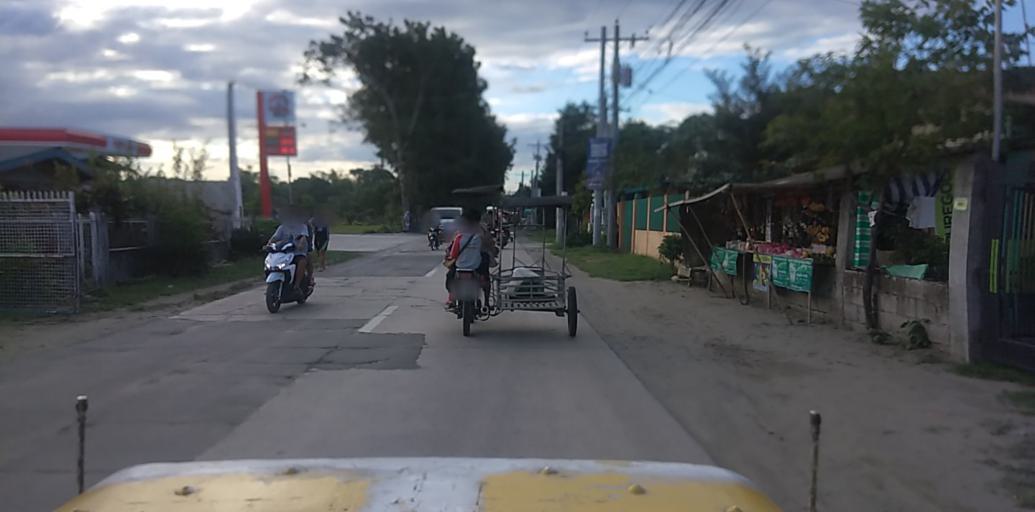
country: PH
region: Central Luzon
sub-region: Province of Pampanga
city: Arayat
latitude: 15.1506
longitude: 120.7462
